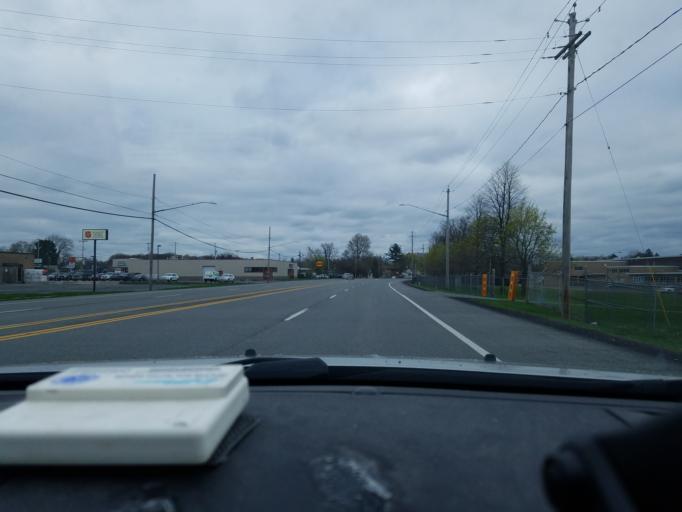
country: US
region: New York
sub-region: Onondaga County
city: North Syracuse
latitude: 43.1201
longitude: -76.1416
